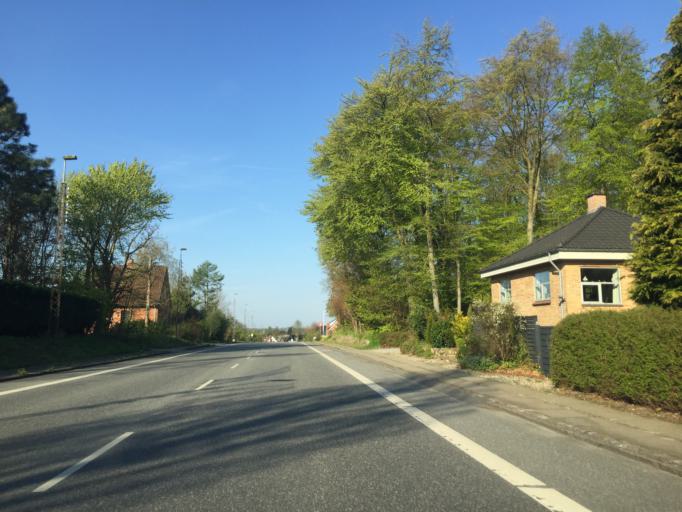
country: DK
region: South Denmark
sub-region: Svendborg Kommune
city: Thuro By
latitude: 55.0753
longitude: 10.6479
